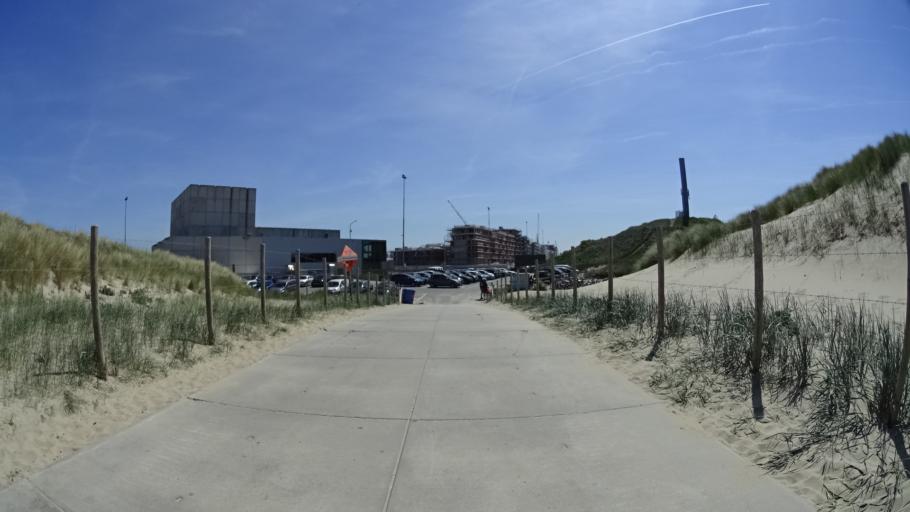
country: NL
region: South Holland
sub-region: Gemeente Den Haag
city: Scheveningen
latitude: 52.0973
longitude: 4.2568
